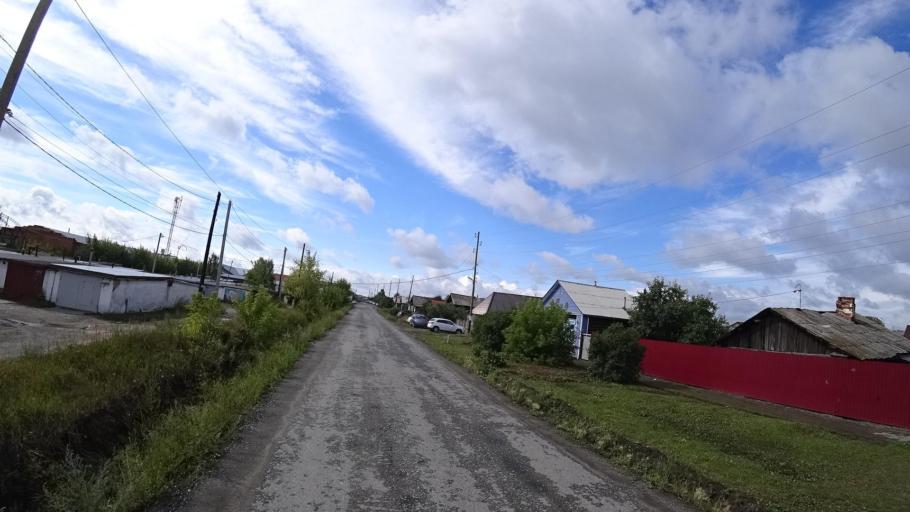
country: RU
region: Sverdlovsk
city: Kamyshlov
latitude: 56.8374
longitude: 62.7277
